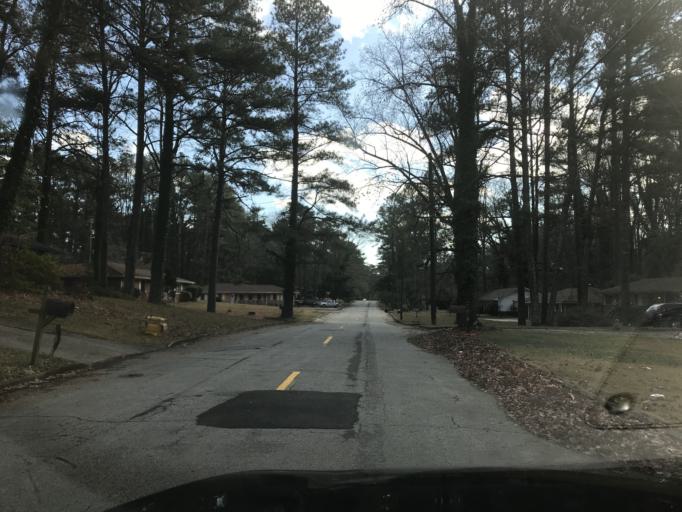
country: US
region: Georgia
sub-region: Fulton County
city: College Park
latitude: 33.6346
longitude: -84.4766
